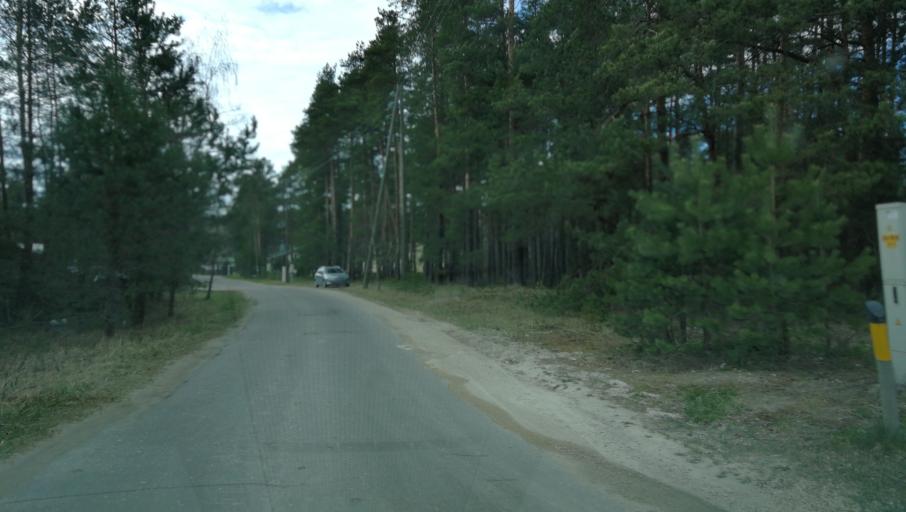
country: LV
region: Garkalne
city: Garkalne
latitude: 57.0413
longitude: 24.4348
